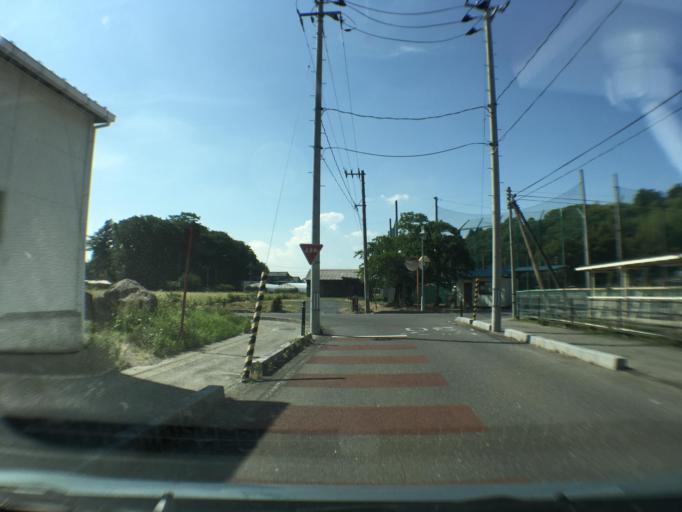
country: JP
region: Miyagi
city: Wakuya
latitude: 38.6578
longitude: 141.2785
